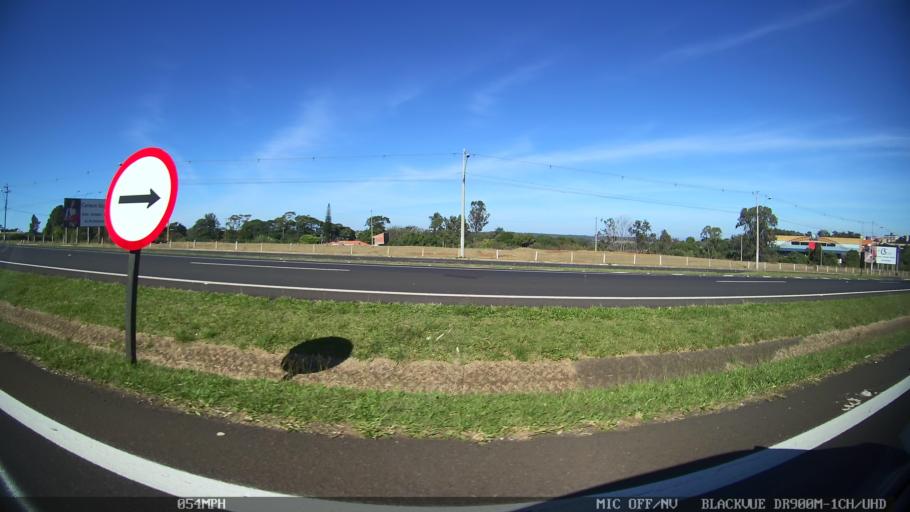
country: BR
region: Sao Paulo
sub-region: Franca
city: Franca
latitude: -20.5696
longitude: -47.3977
